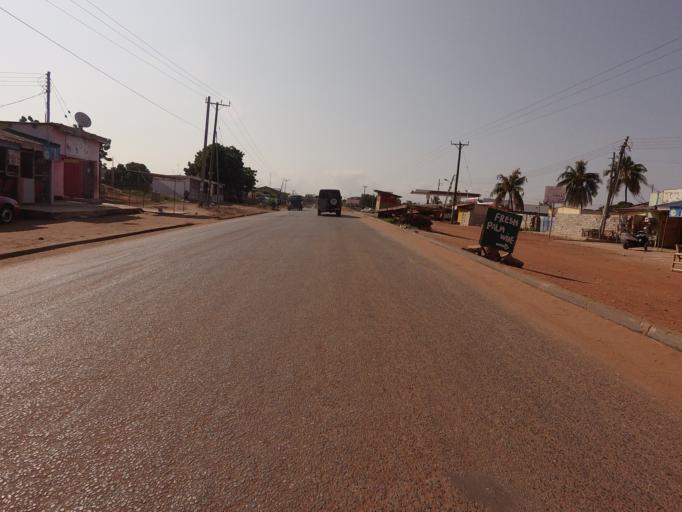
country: GH
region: Greater Accra
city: Teshi Old Town
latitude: 5.5994
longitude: -0.1029
